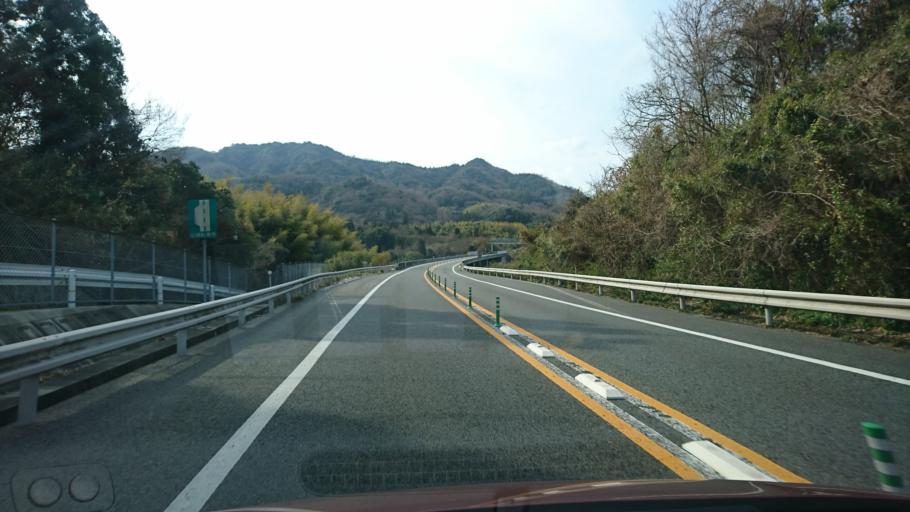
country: JP
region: Hiroshima
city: Innoshima
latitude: 34.1299
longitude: 133.0421
